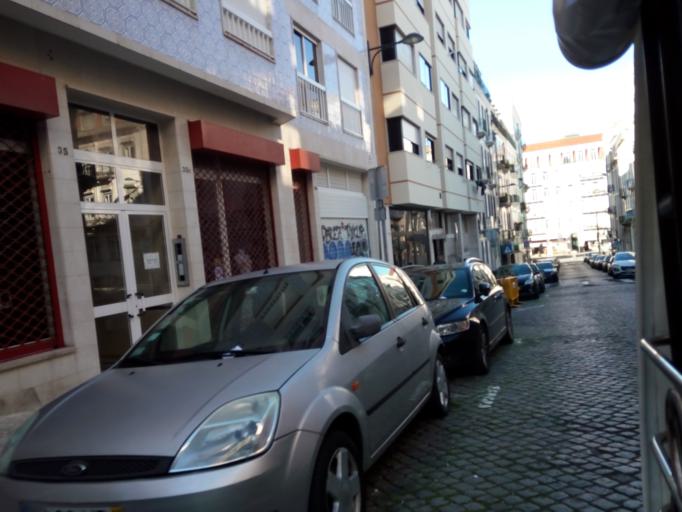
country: PT
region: Lisbon
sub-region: Lisbon
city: Lisbon
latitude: 38.7225
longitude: -9.1341
